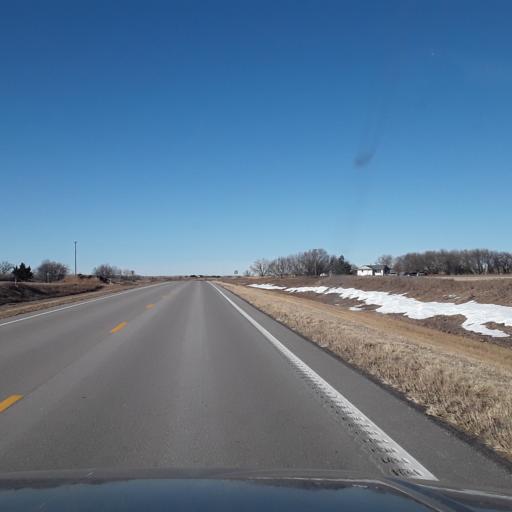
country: US
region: Nebraska
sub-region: Dawson County
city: Cozad
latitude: 40.6750
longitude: -100.1121
